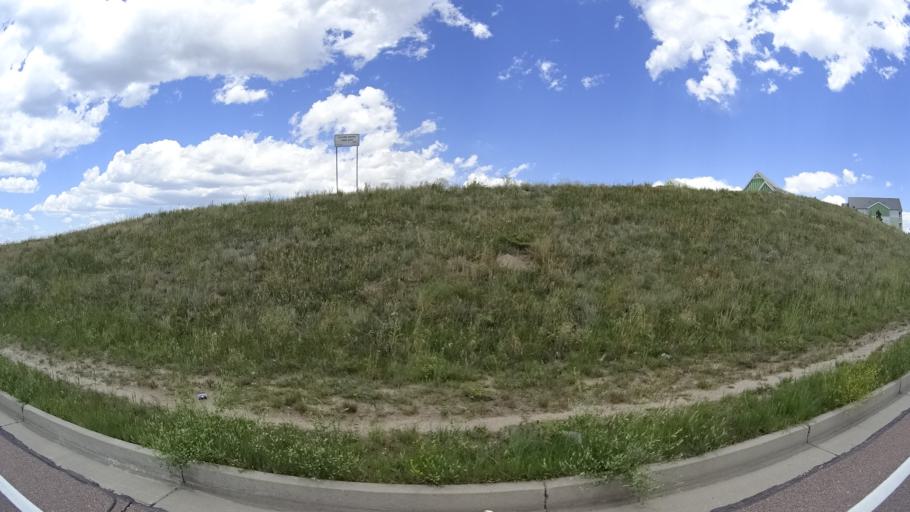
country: US
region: Colorado
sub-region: El Paso County
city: Black Forest
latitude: 38.9426
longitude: -104.7135
